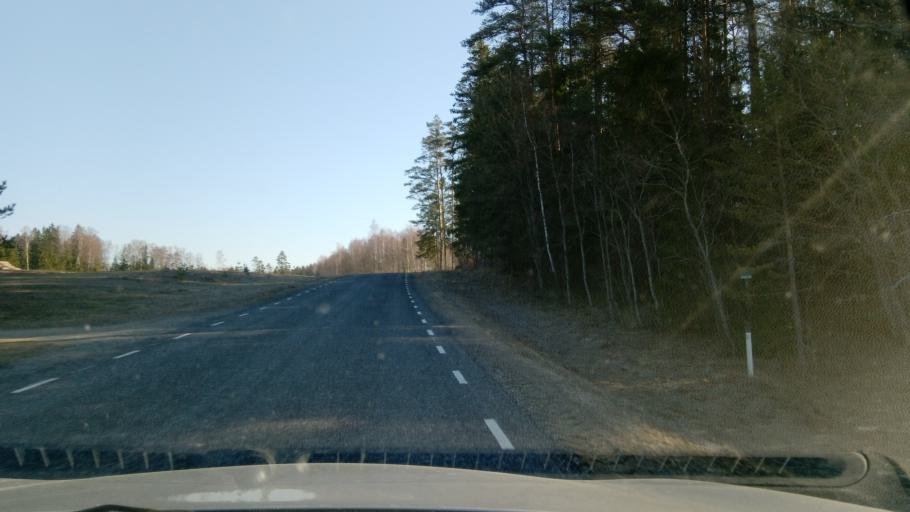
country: EE
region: Laeaene-Virumaa
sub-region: Tamsalu vald
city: Tamsalu
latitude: 59.2116
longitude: 26.1517
